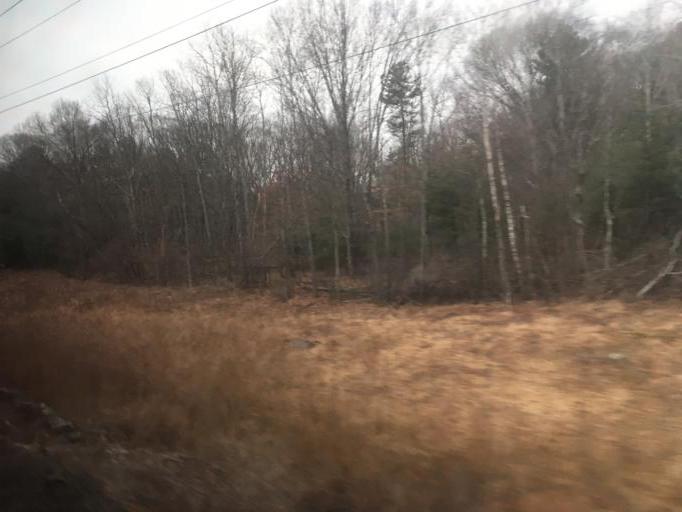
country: US
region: Massachusetts
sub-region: Norfolk County
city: Canton
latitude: 42.1544
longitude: -71.1556
